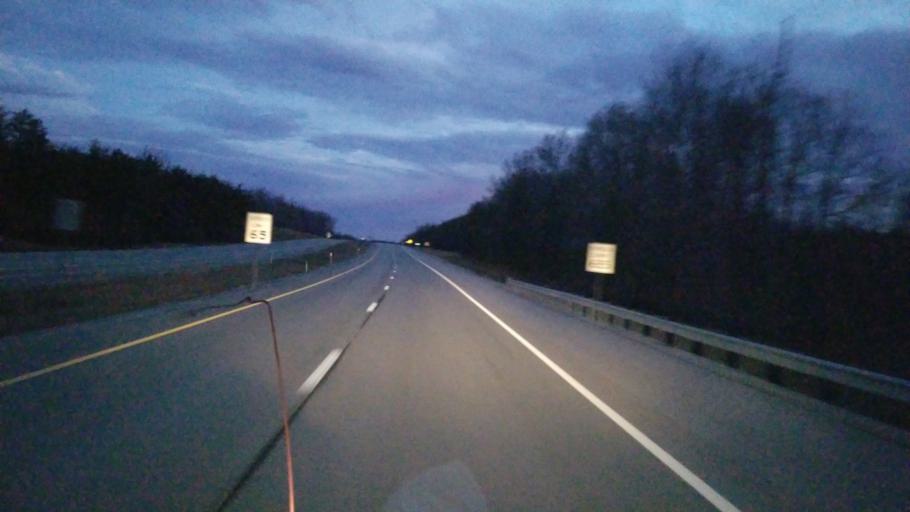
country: US
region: Tennessee
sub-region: Sequatchie County
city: Dunlap
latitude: 35.5445
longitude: -85.4685
